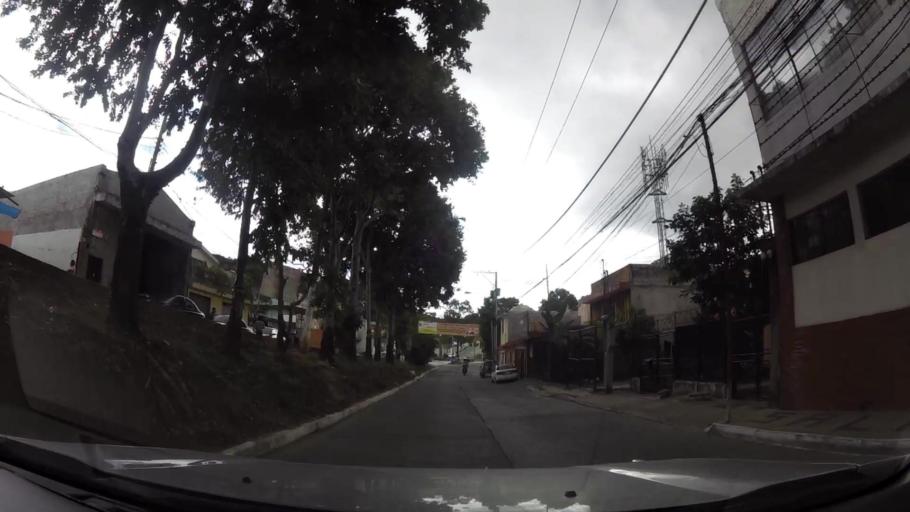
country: GT
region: Guatemala
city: Guatemala City
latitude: 14.6739
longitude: -90.5548
